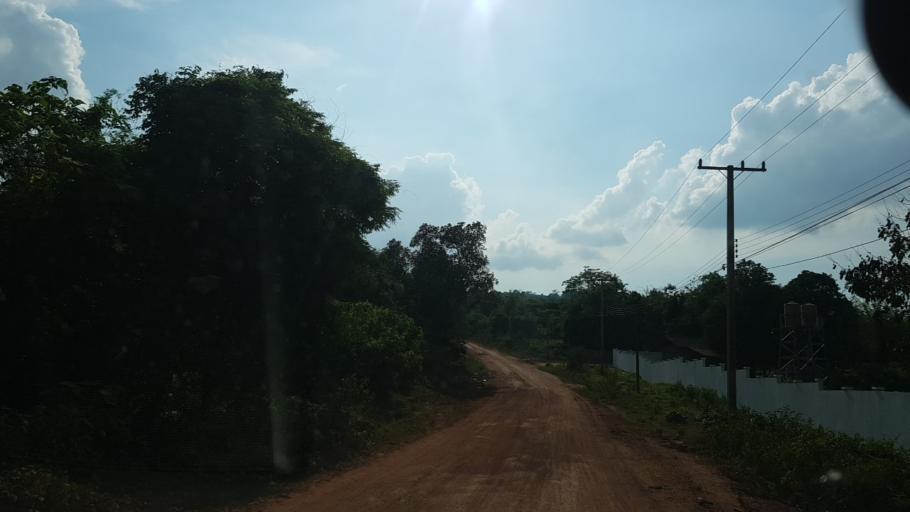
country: LA
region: Vientiane
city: Muang Phon-Hong
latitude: 18.3502
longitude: 102.2703
